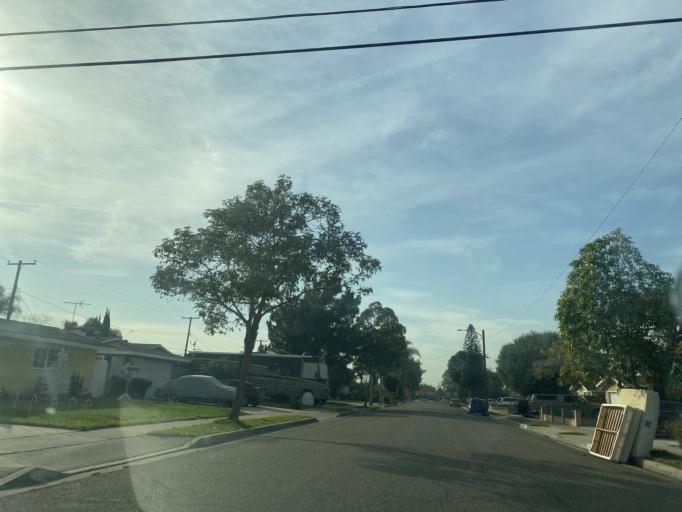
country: US
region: California
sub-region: Orange County
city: Fullerton
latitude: 33.8513
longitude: -117.9560
